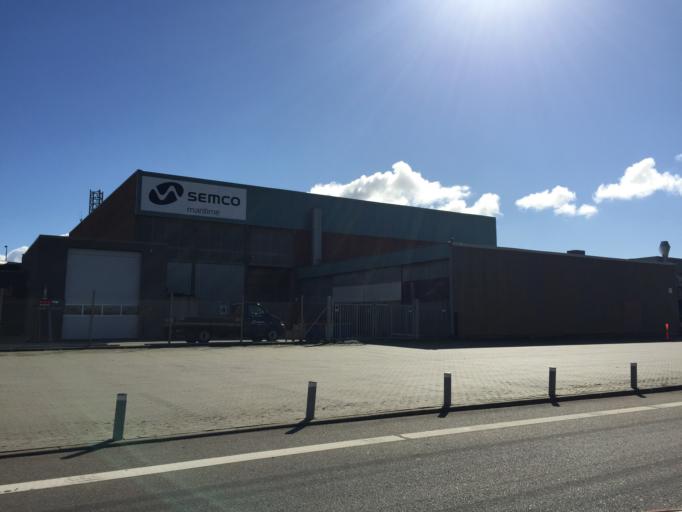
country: DK
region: South Denmark
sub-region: Esbjerg Kommune
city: Esbjerg
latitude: 55.4811
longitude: 8.4164
